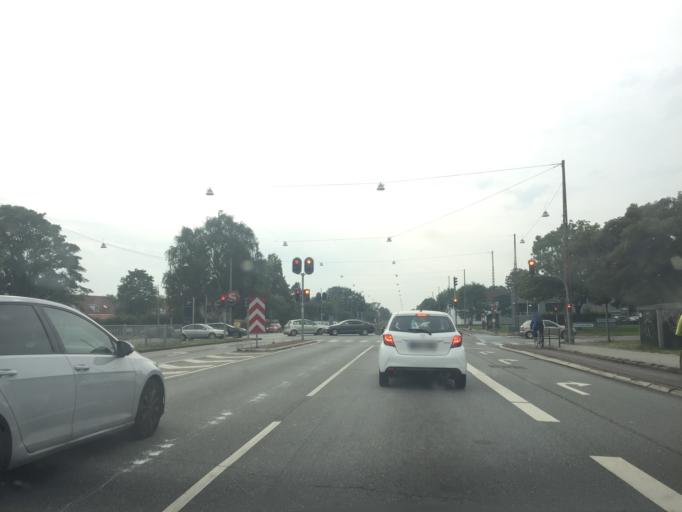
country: DK
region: Capital Region
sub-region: Albertslund Kommune
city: Albertslund
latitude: 55.6624
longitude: 12.3518
